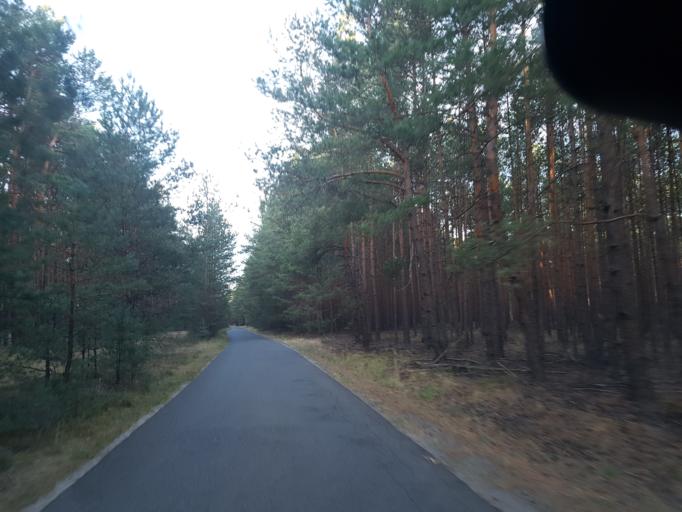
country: DE
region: Brandenburg
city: Hohenbucko
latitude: 51.7437
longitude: 13.5162
